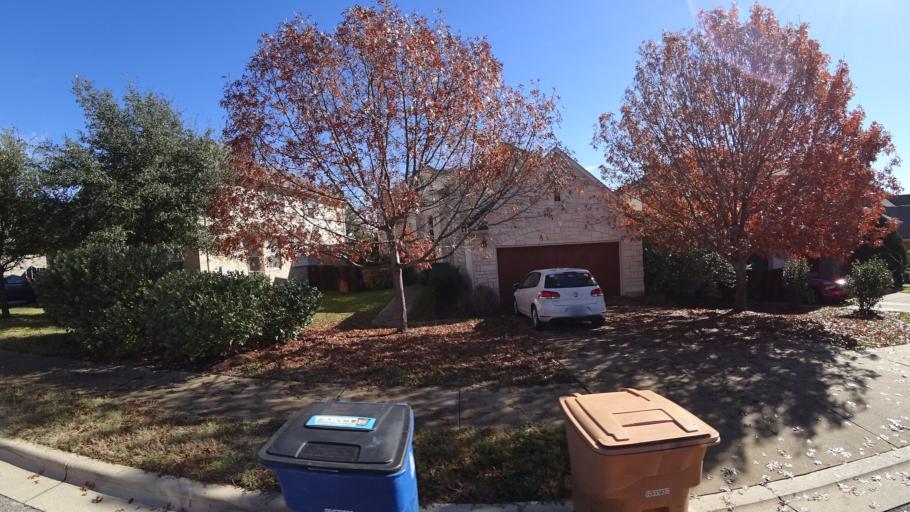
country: US
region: Texas
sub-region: Travis County
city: Wells Branch
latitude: 30.4233
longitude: -97.7068
